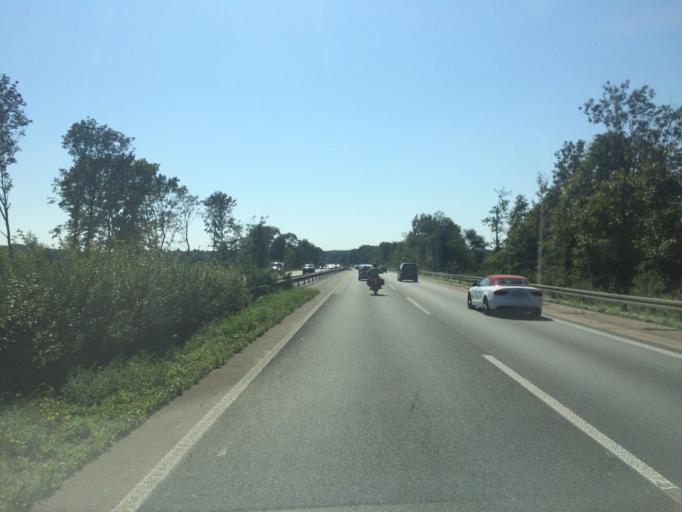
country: DE
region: North Rhine-Westphalia
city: Bergkamen
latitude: 51.6375
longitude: 7.6856
